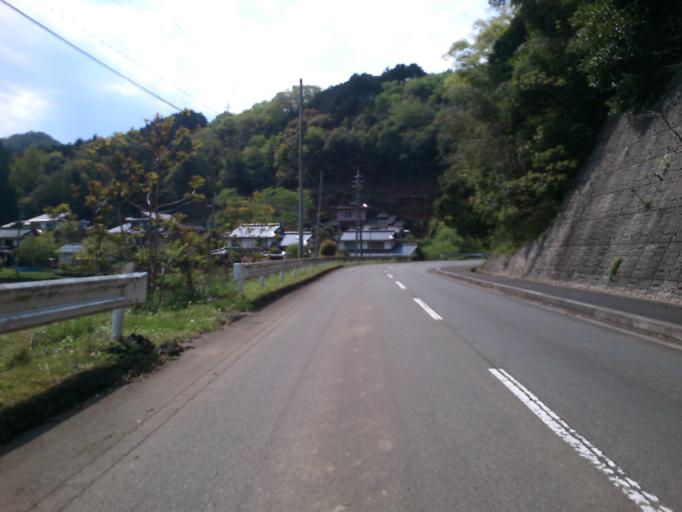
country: JP
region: Kyoto
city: Fukuchiyama
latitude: 35.3307
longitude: 134.9334
